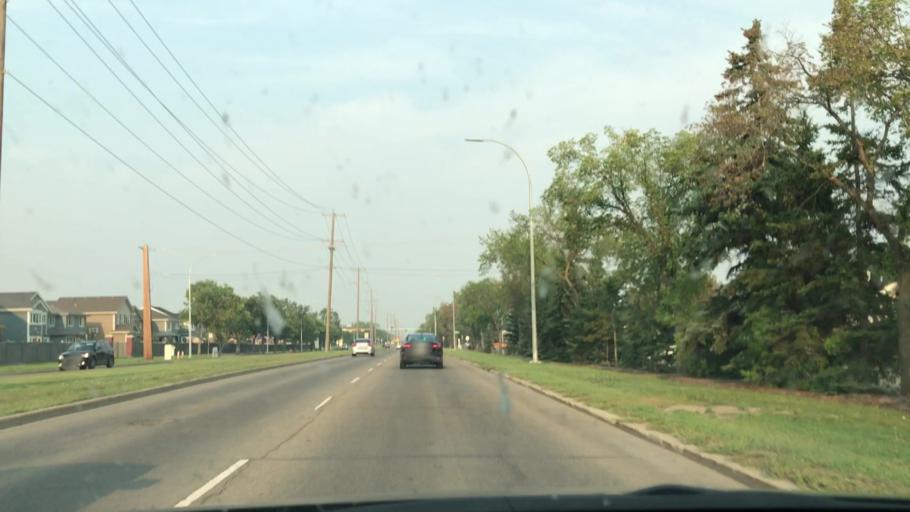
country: CA
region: Alberta
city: Edmonton
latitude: 53.5994
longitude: -113.5089
